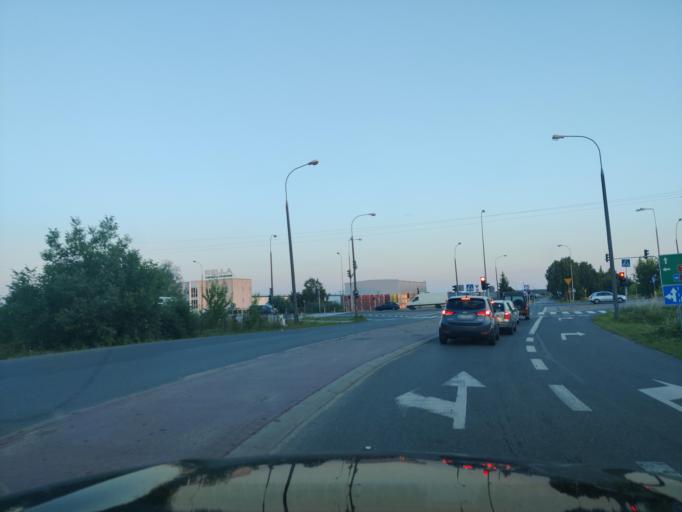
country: PL
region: Masovian Voivodeship
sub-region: Powiat nowodworski
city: Nowy Dwor Mazowiecki
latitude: 52.3883
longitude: 20.7384
